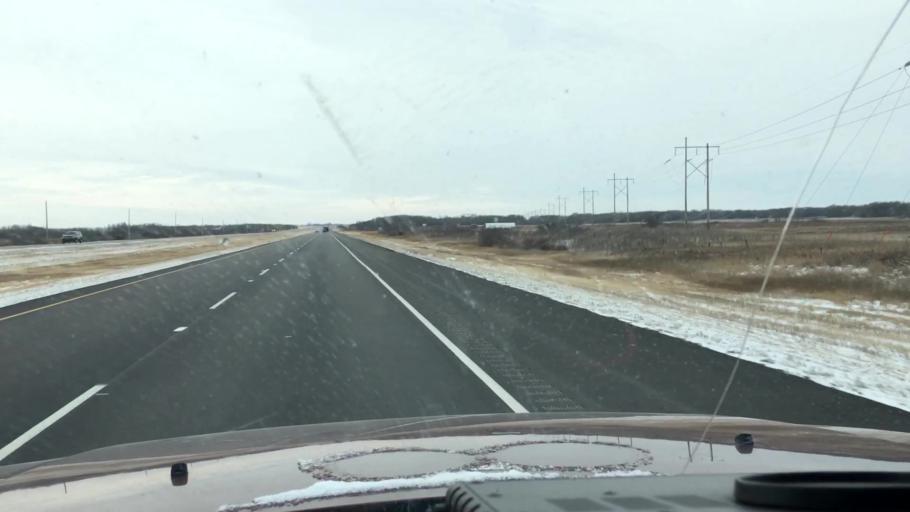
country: CA
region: Saskatchewan
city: Saskatoon
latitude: 51.8877
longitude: -106.5157
